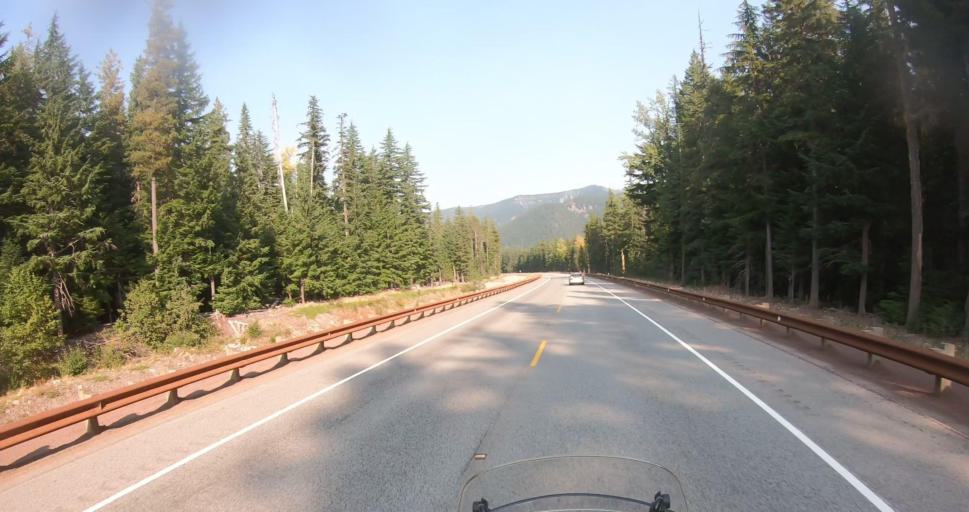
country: US
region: Oregon
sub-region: Hood River County
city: Odell
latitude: 45.3223
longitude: -121.5991
